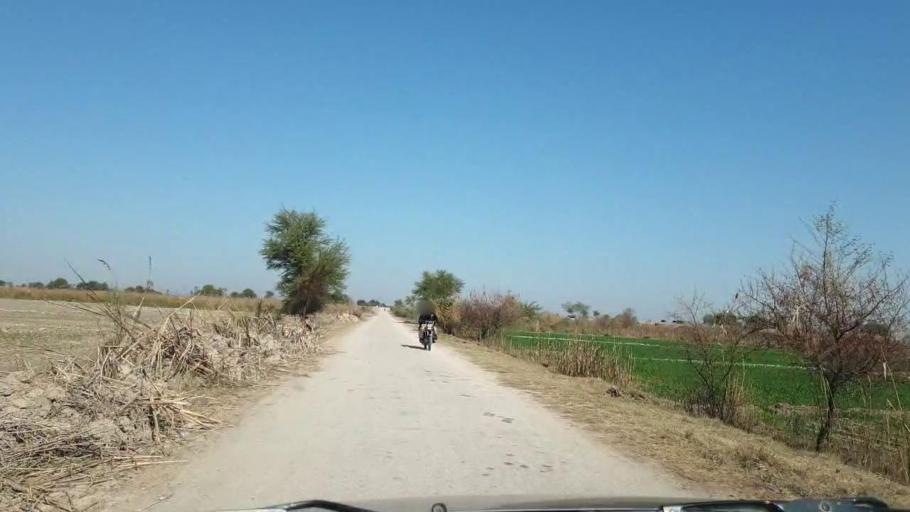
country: PK
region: Sindh
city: Sinjhoro
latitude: 26.1029
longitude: 68.8428
